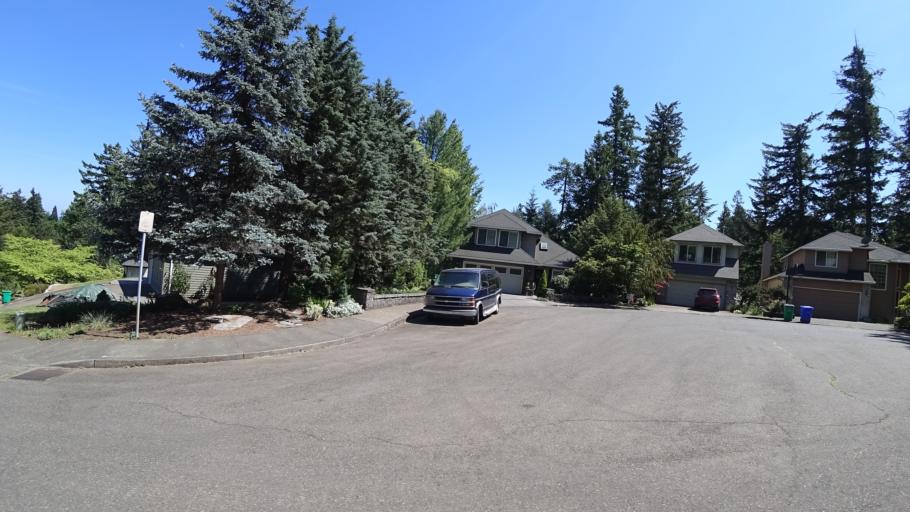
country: US
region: Oregon
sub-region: Washington County
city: Metzger
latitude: 45.4467
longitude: -122.7200
